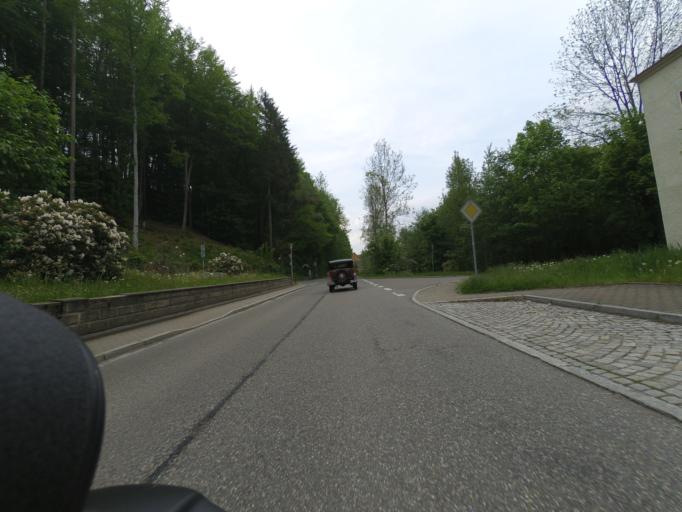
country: DE
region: Saxony
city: Scharfenstein
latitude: 50.6994
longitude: 13.0578
